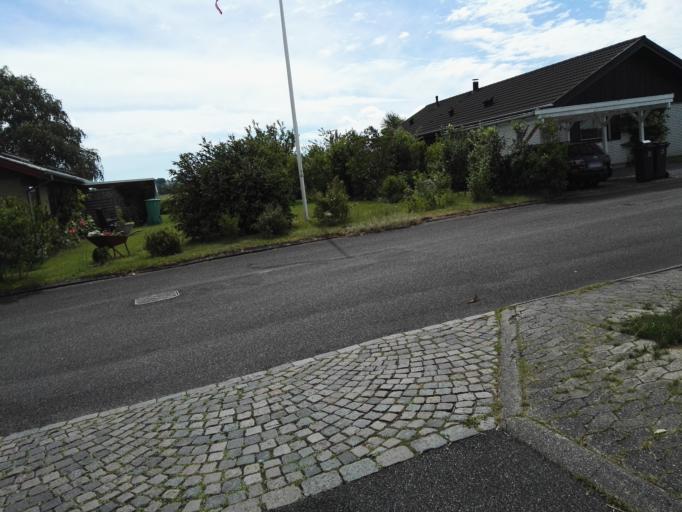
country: DK
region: Capital Region
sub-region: Frederikssund Kommune
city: Slangerup
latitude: 55.8406
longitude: 12.1794
